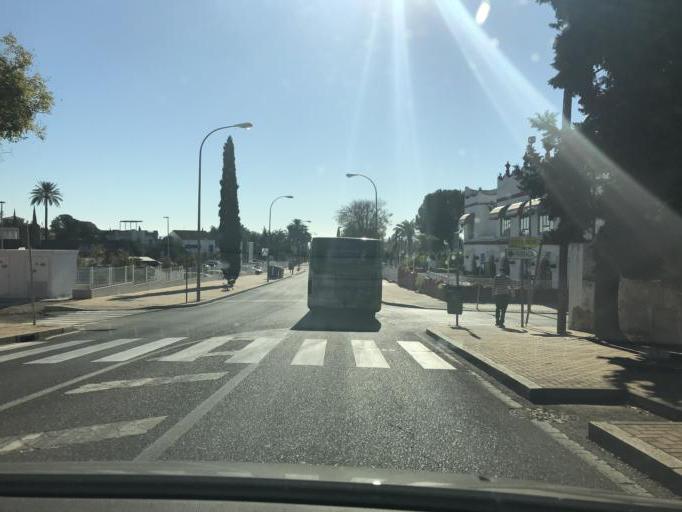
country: ES
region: Andalusia
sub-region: Province of Cordoba
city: Cordoba
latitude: 37.9046
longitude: -4.7906
